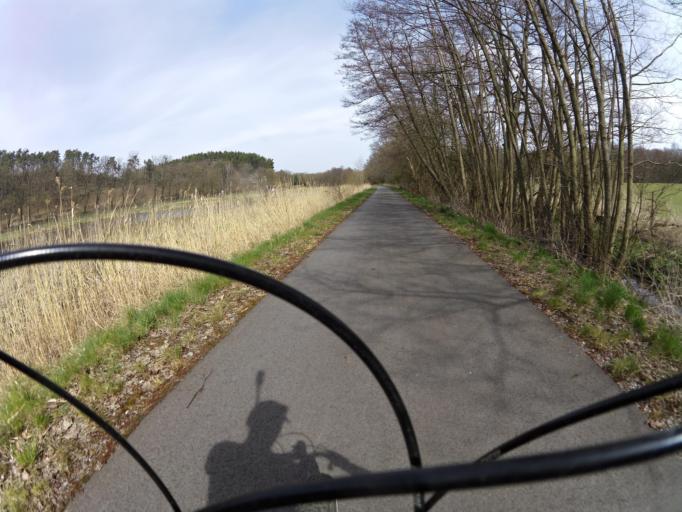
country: PL
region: West Pomeranian Voivodeship
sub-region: Powiat gryfinski
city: Cedynia
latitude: 52.8300
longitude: 14.2466
